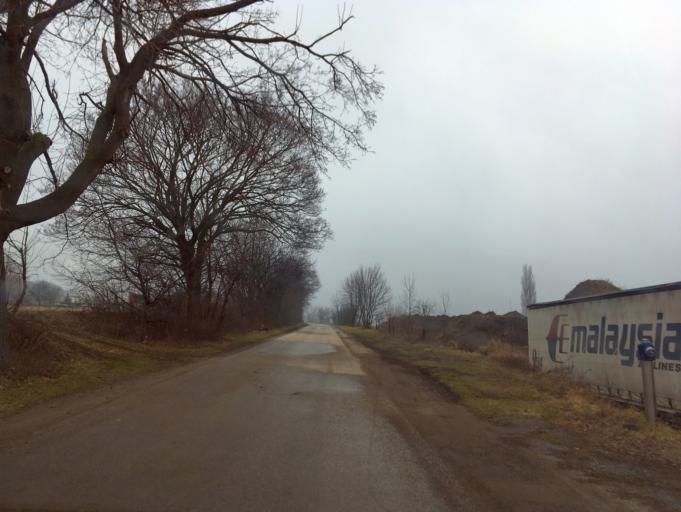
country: AT
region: Lower Austria
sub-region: Politischer Bezirk Bruck an der Leitha
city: Trautmannsdorf an der Leitha
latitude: 48.0386
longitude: 16.6802
